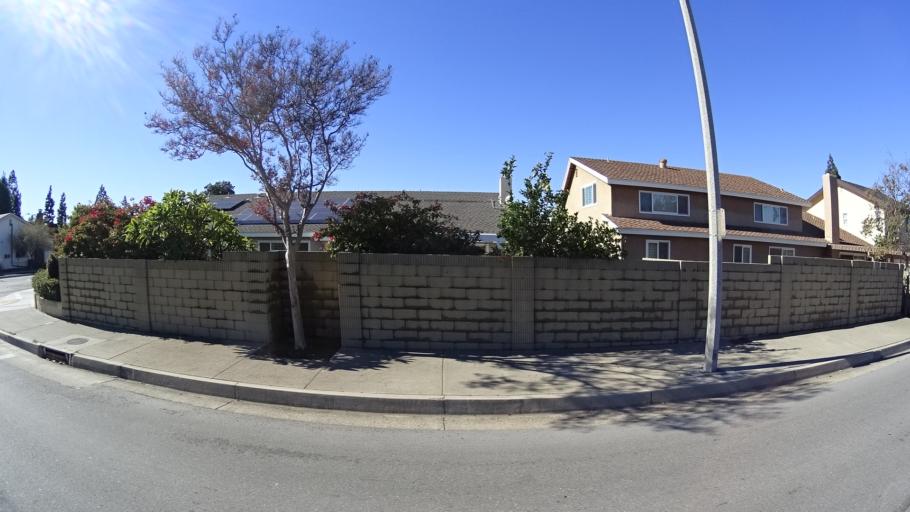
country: US
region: California
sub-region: Orange County
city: Placentia
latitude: 33.8905
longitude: -117.8549
